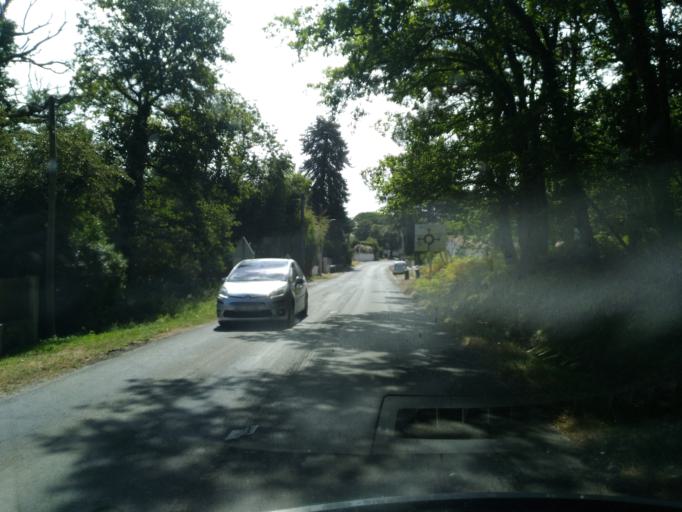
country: FR
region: Poitou-Charentes
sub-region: Departement de la Charente-Maritime
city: Vaux-sur-Mer
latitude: 45.6654
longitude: -1.0738
